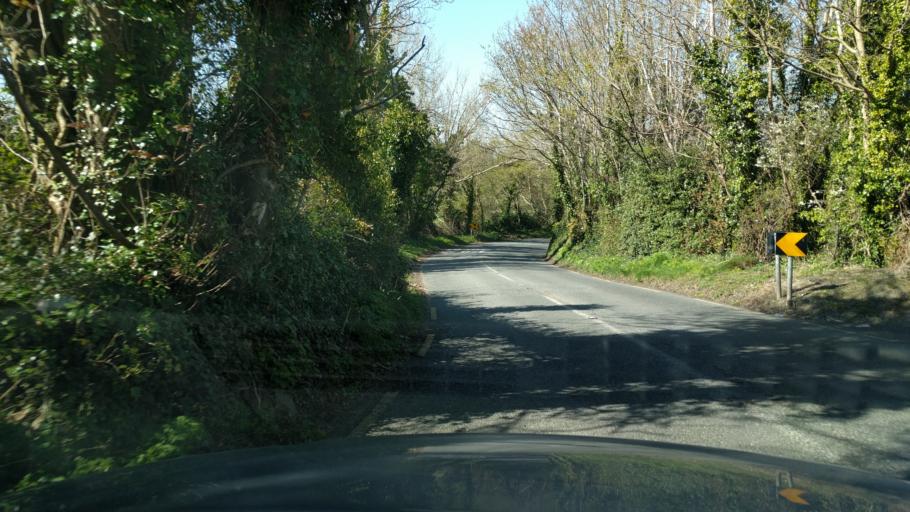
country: IE
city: Knocklyon
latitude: 53.2640
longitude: -6.3236
